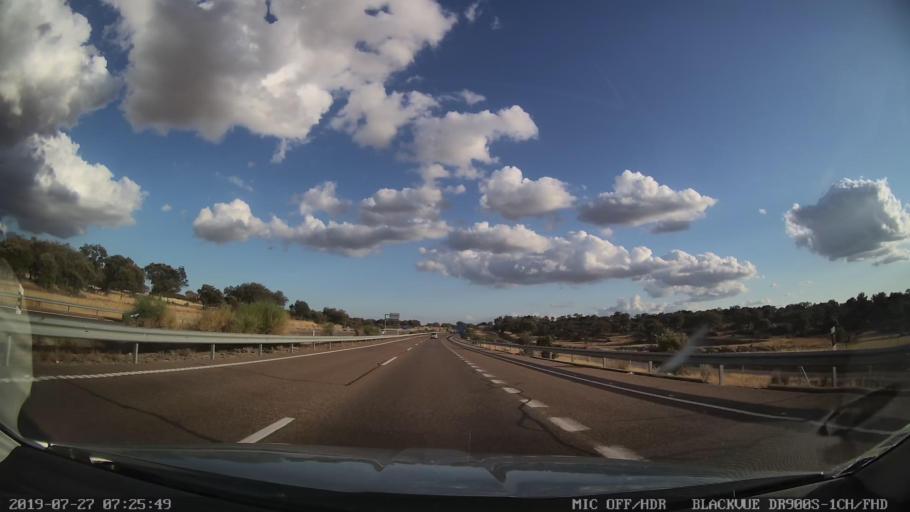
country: ES
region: Extremadura
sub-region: Provincia de Caceres
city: Villamesias
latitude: 39.2697
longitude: -5.8569
